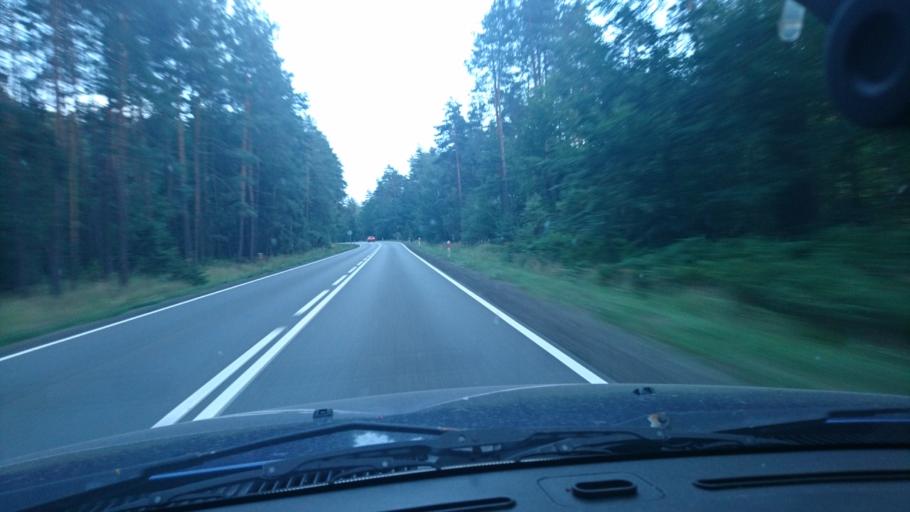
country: PL
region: Silesian Voivodeship
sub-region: Powiat tarnogorski
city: Tworog
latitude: 50.4979
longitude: 18.7710
